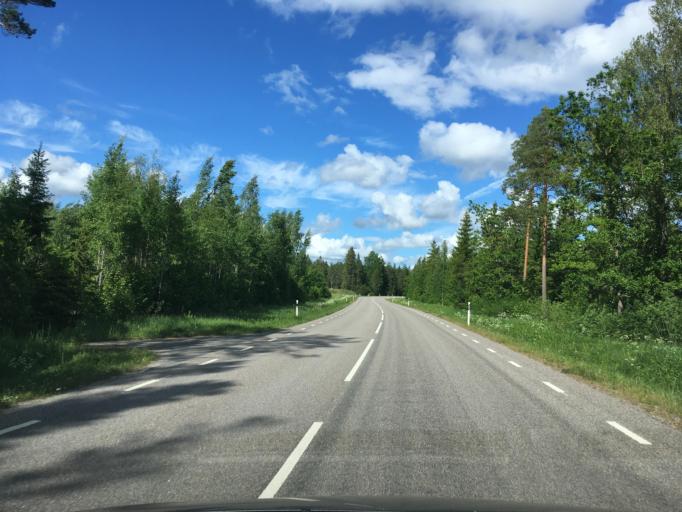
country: EE
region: Paernumaa
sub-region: Halinga vald
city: Parnu-Jaagupi
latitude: 58.6720
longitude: 24.5935
